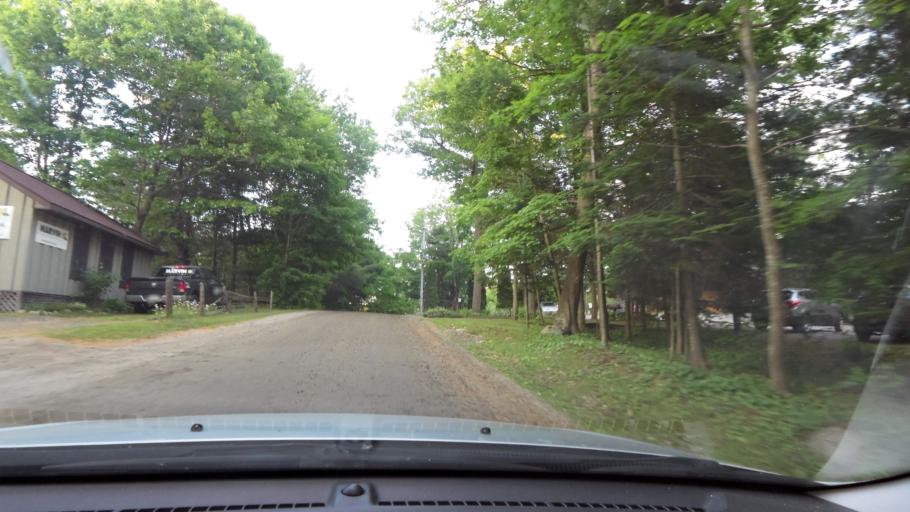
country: CA
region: Ontario
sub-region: Parry Sound District
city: Parry Sound
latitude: 45.3220
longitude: -79.9853
